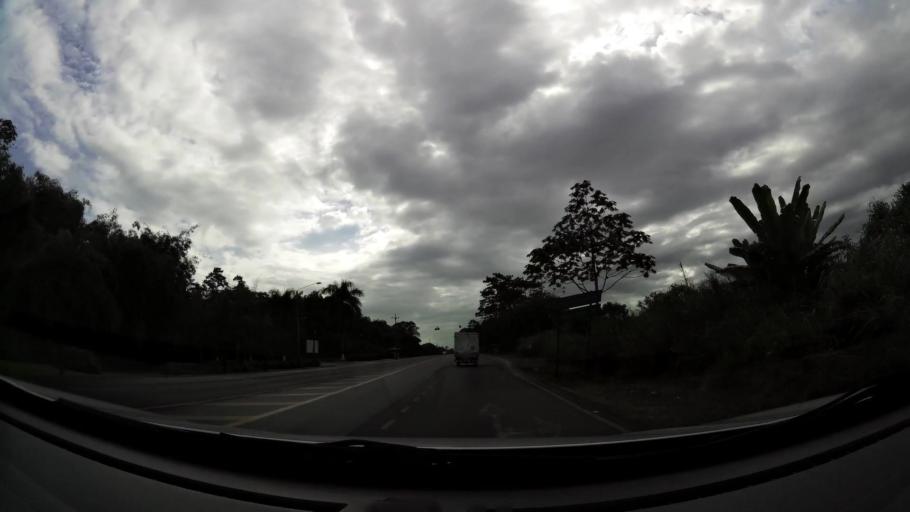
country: CR
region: Limon
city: Pocora
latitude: 10.1767
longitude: -83.6170
